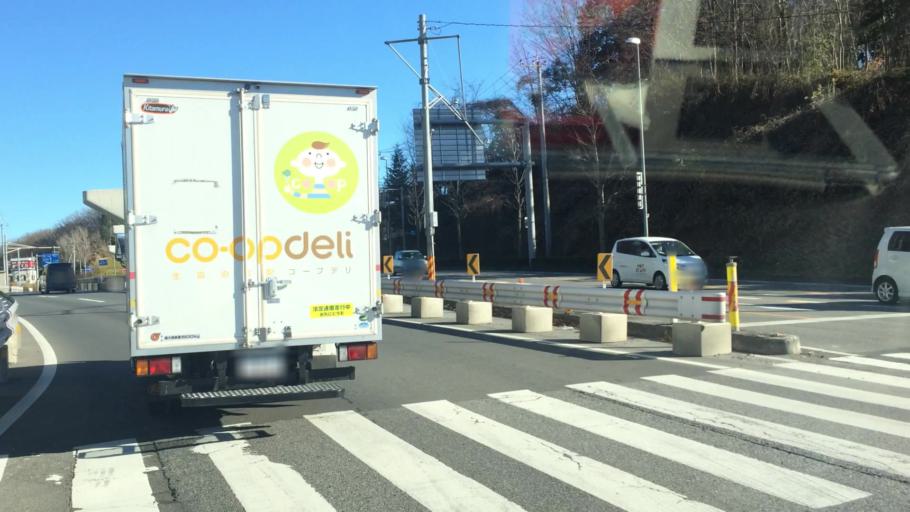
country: JP
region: Tochigi
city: Utsunomiya-shi
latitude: 36.5930
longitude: 139.8682
